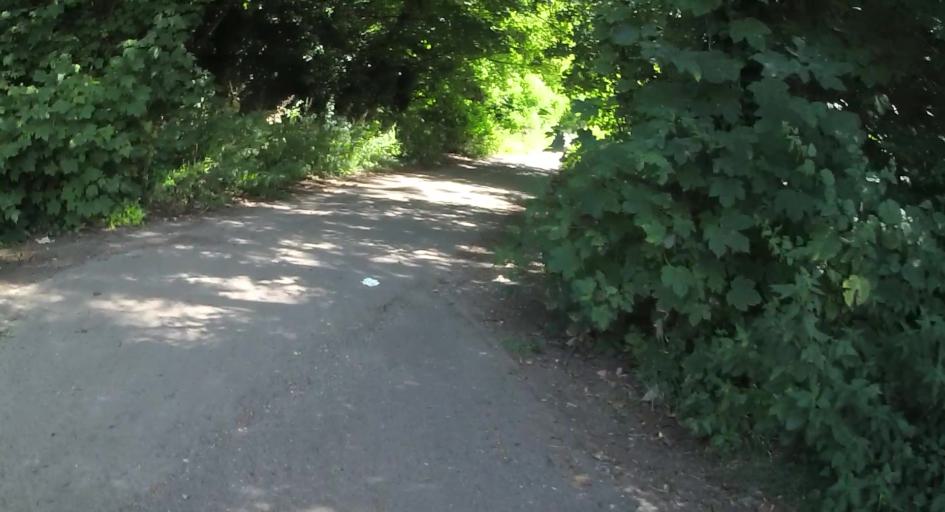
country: GB
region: England
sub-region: Hampshire
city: Winchester
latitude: 51.0388
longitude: -1.3183
